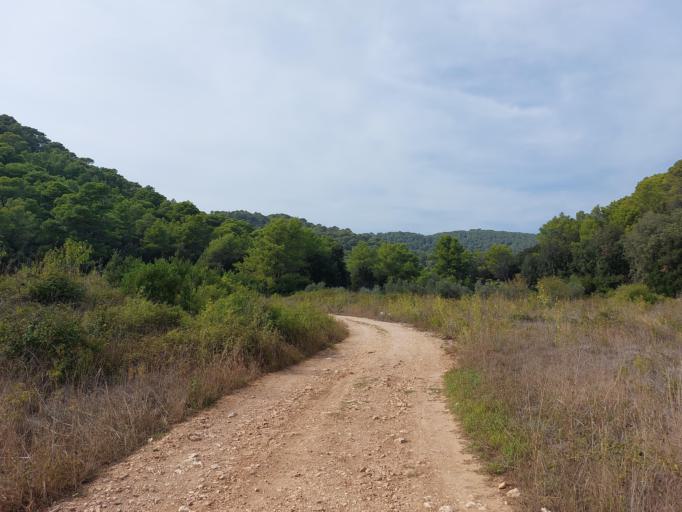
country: HR
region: Dubrovacko-Neretvanska
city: Smokvica
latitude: 42.7500
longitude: 16.8364
